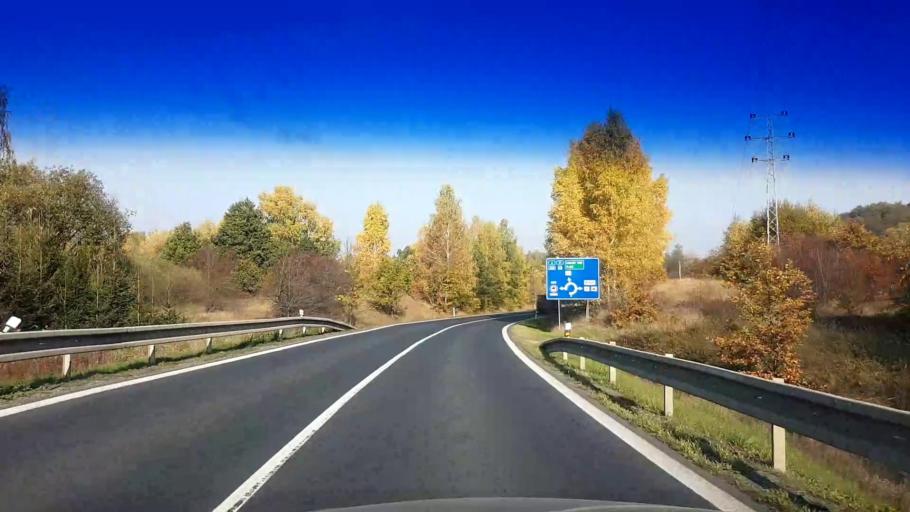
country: CZ
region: Karlovarsky
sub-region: Okres Cheb
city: Cheb
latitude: 50.0725
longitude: 12.3900
